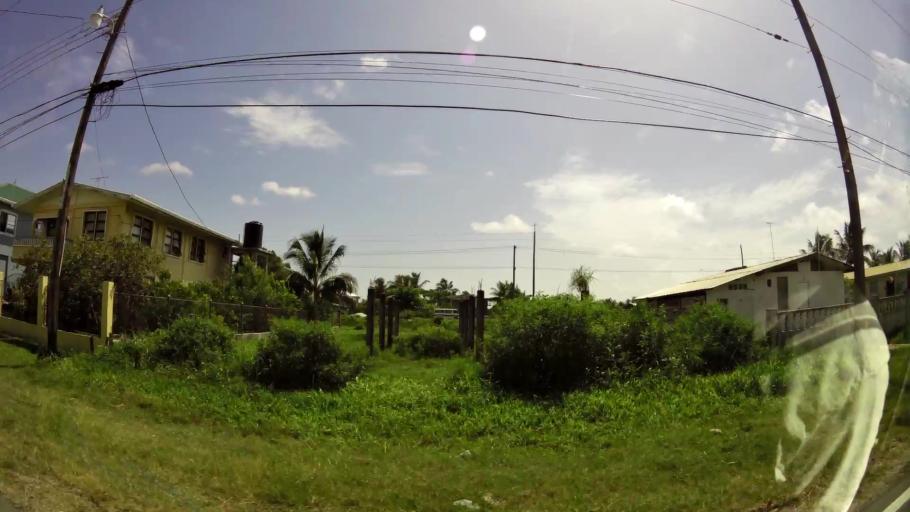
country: GY
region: Demerara-Mahaica
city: Mahaica Village
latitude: 6.7725
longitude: -58.0081
